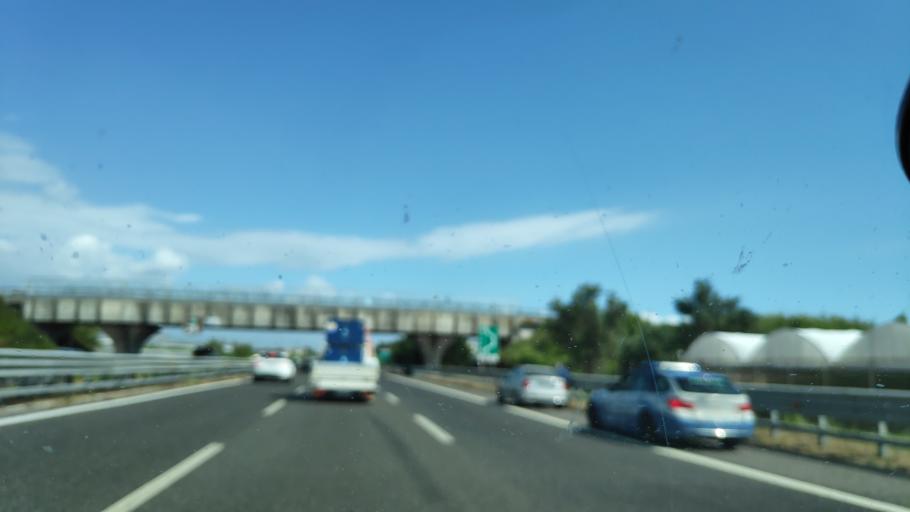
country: IT
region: Campania
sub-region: Provincia di Salerno
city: Sant'Antonio
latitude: 40.6432
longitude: 14.8946
